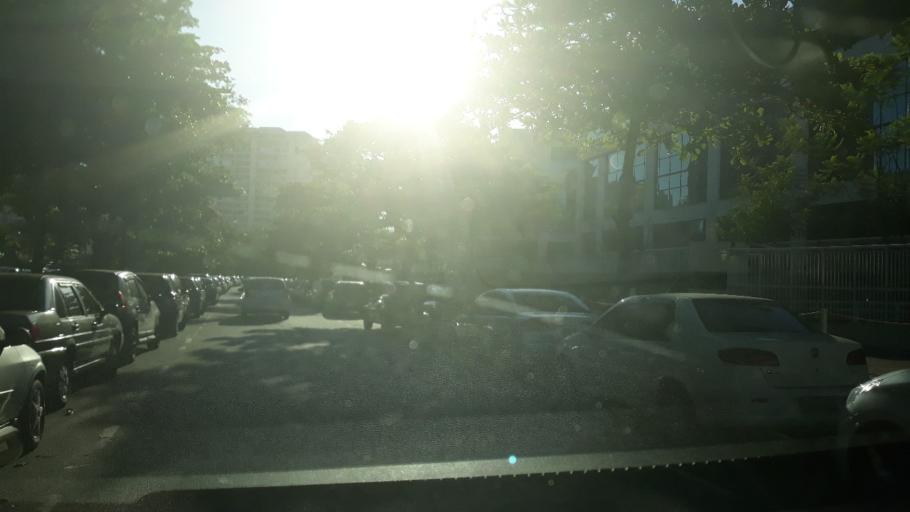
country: BR
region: Rio de Janeiro
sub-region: Rio De Janeiro
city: Rio de Janeiro
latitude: -23.0015
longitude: -43.3482
